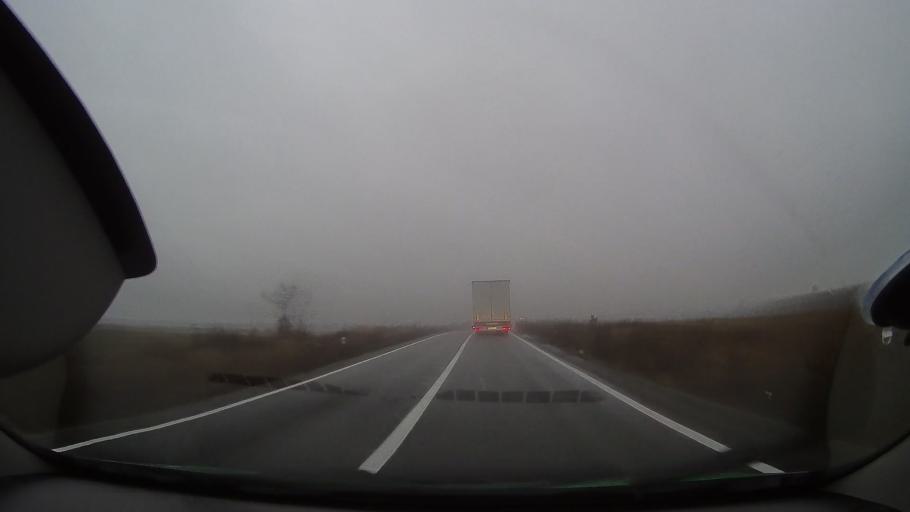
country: RO
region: Bihor
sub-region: Comuna Olcea
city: Olcea
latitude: 46.6633
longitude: 21.9629
